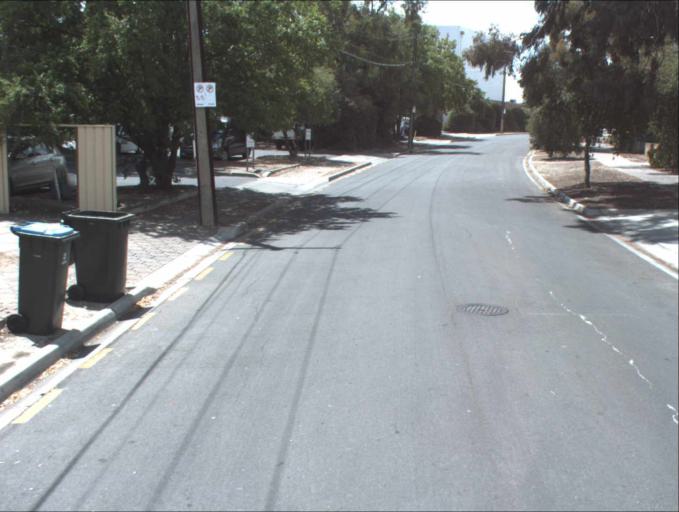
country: AU
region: South Australia
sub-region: Port Adelaide Enfield
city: Gilles Plains
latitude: -34.8569
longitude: 138.6574
